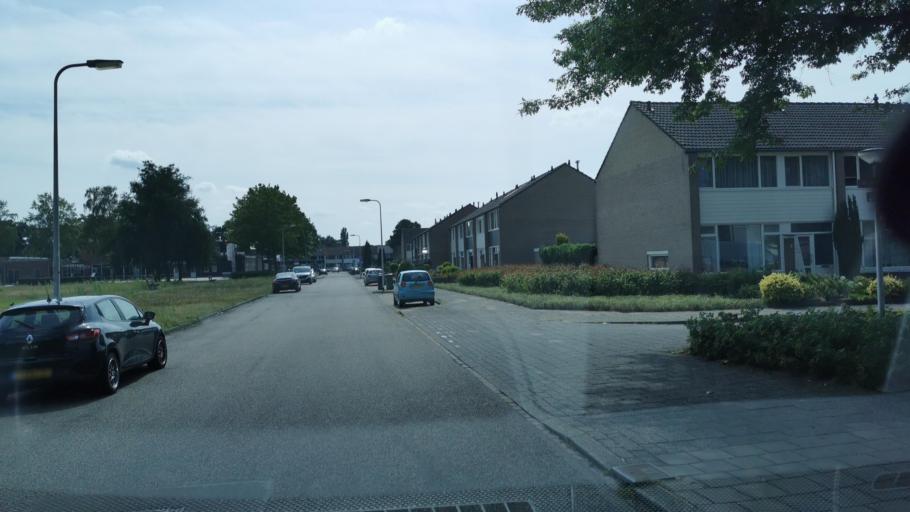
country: NL
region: Overijssel
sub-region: Gemeente Enschede
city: Enschede
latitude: 52.1885
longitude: 6.8802
